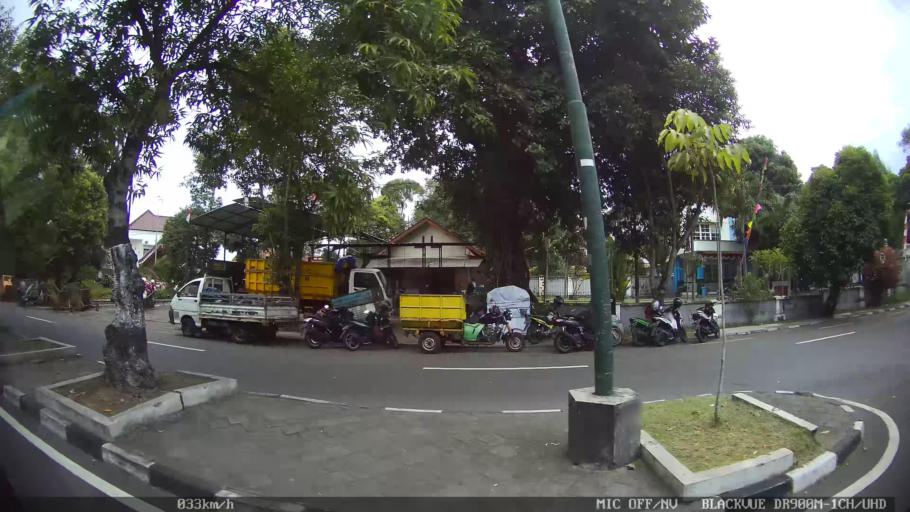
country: ID
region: Daerah Istimewa Yogyakarta
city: Yogyakarta
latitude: -7.7956
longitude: 110.3830
